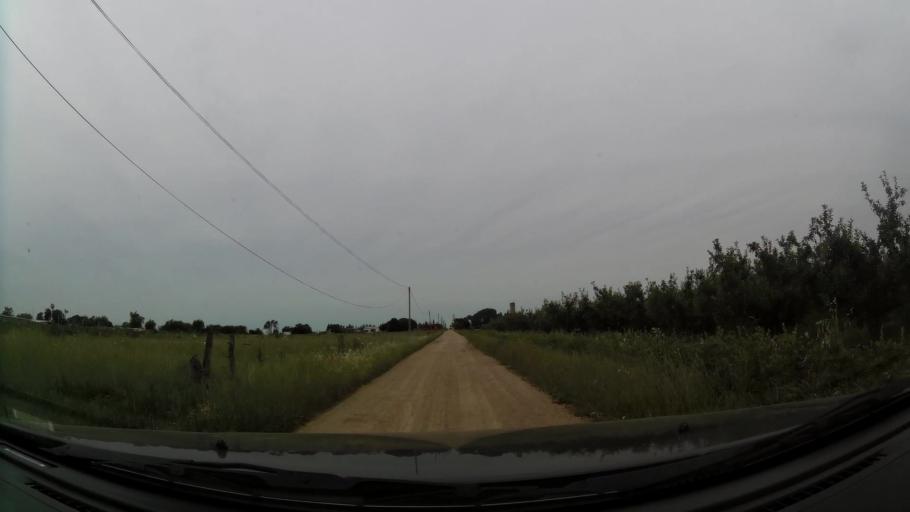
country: UY
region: Canelones
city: Las Piedras
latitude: -34.7418
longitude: -56.2354
